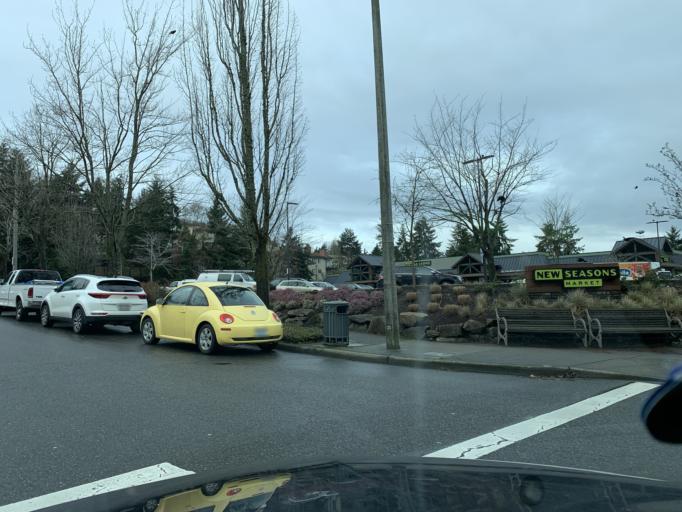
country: US
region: Washington
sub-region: King County
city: Mercer Island
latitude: 47.5843
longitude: -122.2351
